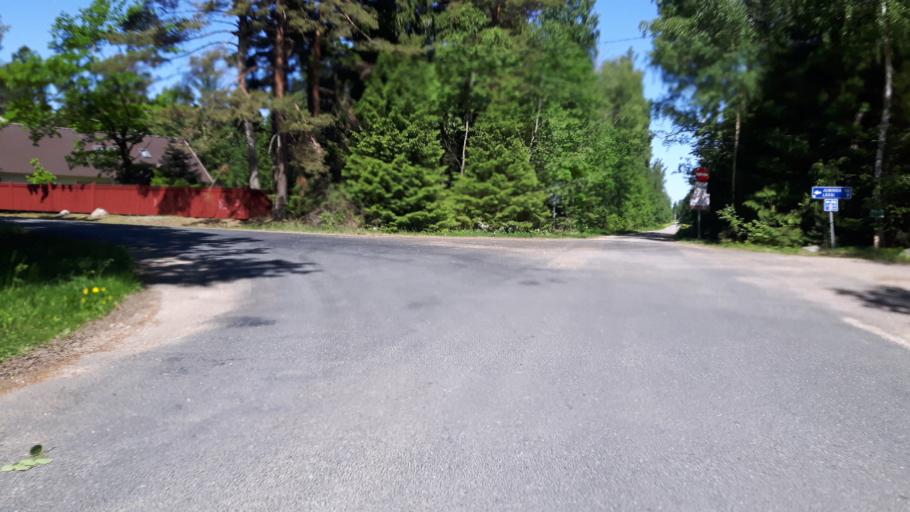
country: EE
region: Harju
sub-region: Loksa linn
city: Loksa
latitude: 59.5774
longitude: 25.6107
